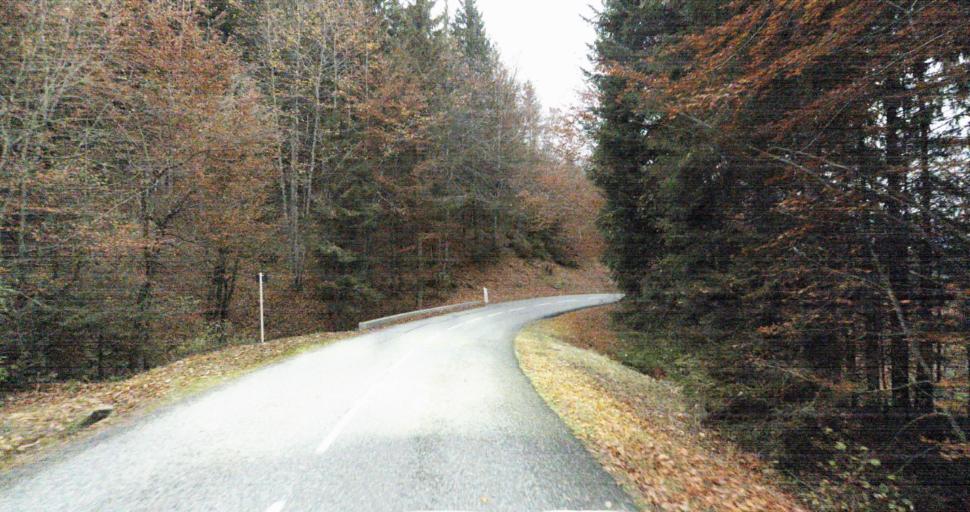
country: FR
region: Rhone-Alpes
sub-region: Departement de la Haute-Savoie
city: Saint-Jorioz
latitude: 45.8042
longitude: 6.1362
